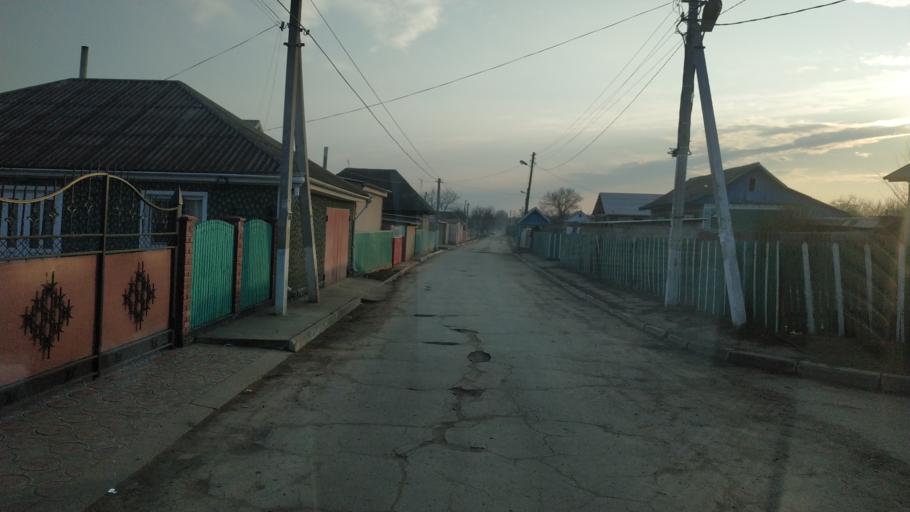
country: MD
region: Hincesti
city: Dancu
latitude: 46.7168
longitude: 28.3513
